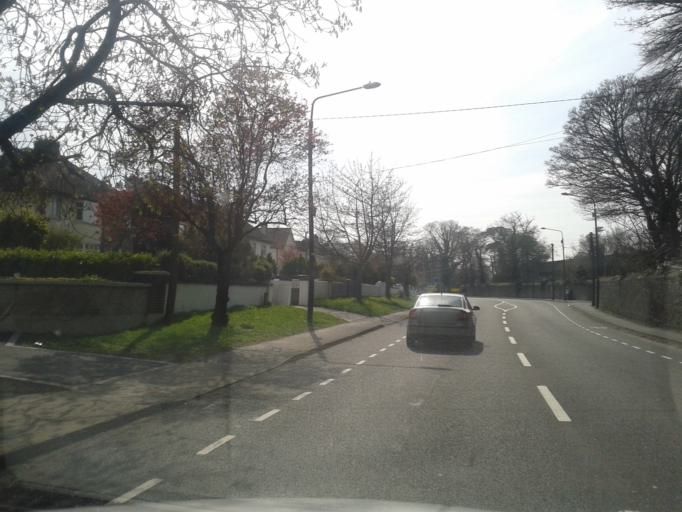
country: IE
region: Leinster
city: Beaumont
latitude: 53.4017
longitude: -6.2421
